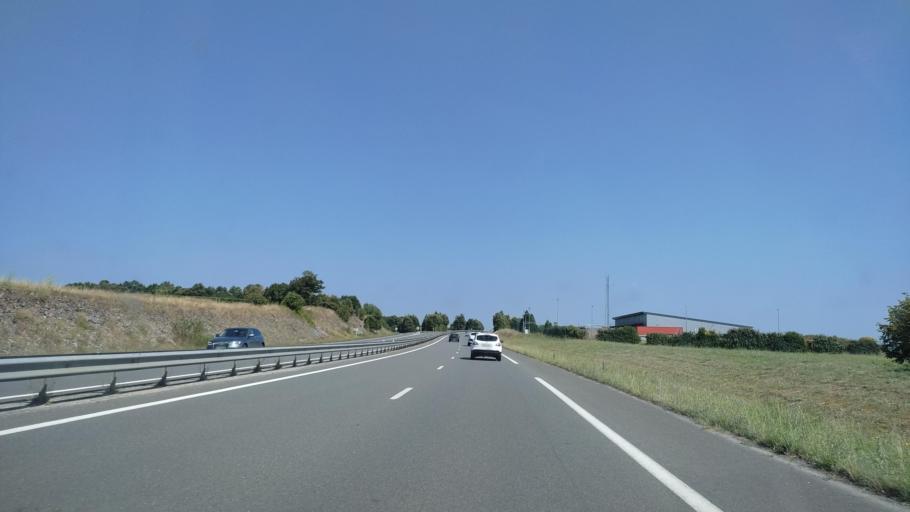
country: FR
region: Poitou-Charentes
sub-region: Departement de la Charente
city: Gensac-la-Pallue
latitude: 45.6651
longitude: -0.2369
